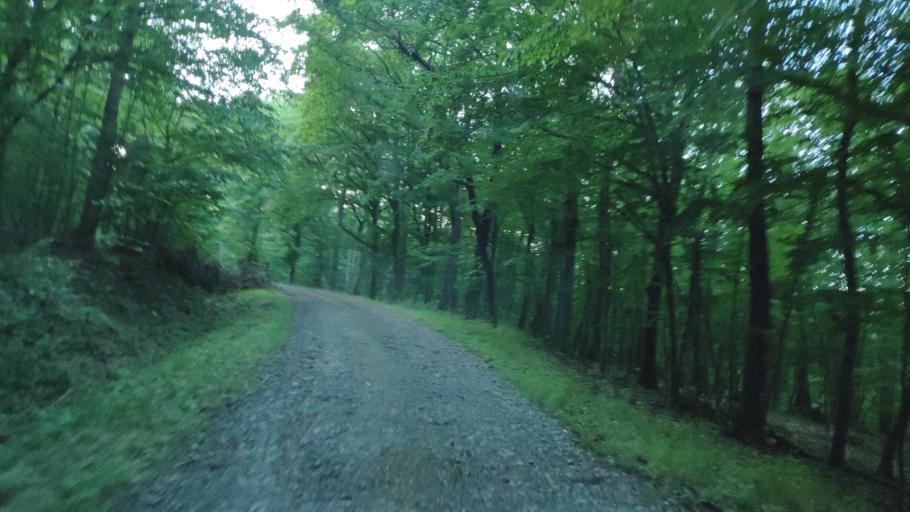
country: SK
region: Kosicky
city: Secovce
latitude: 48.5836
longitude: 21.5340
